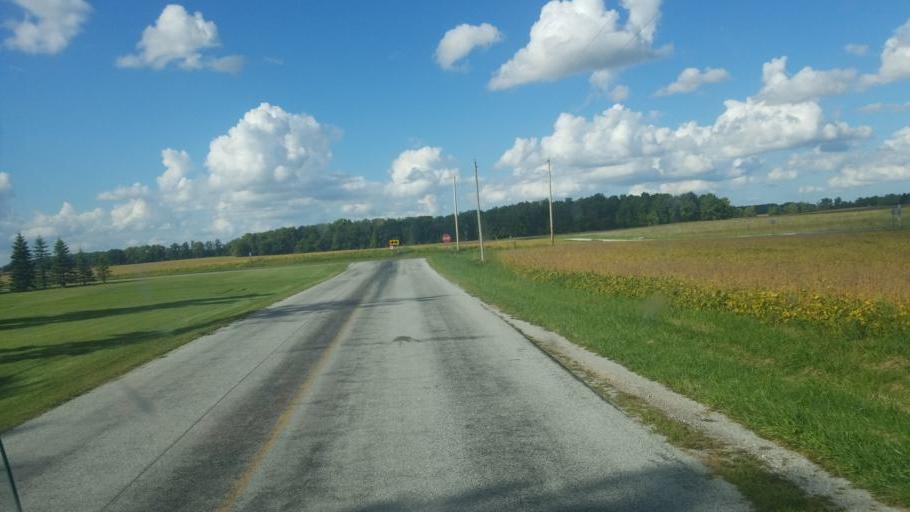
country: US
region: Ohio
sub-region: Hardin County
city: Ada
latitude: 40.7318
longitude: -83.7297
